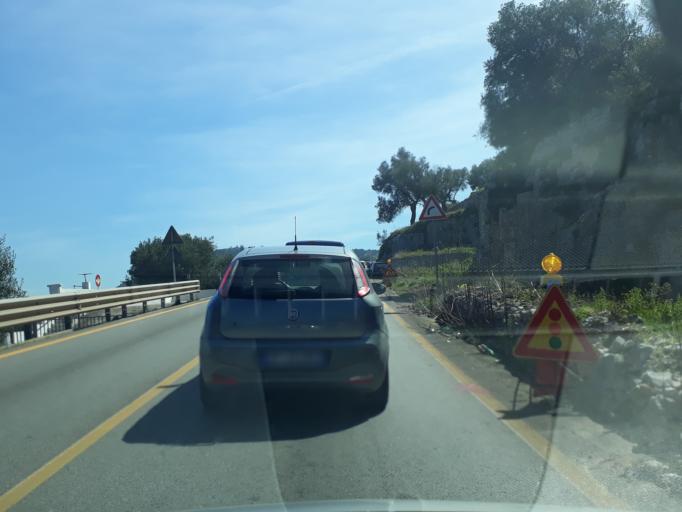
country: IT
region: Apulia
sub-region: Provincia di Brindisi
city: Lamie di Olimpie-Selva
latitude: 40.8148
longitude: 17.3458
